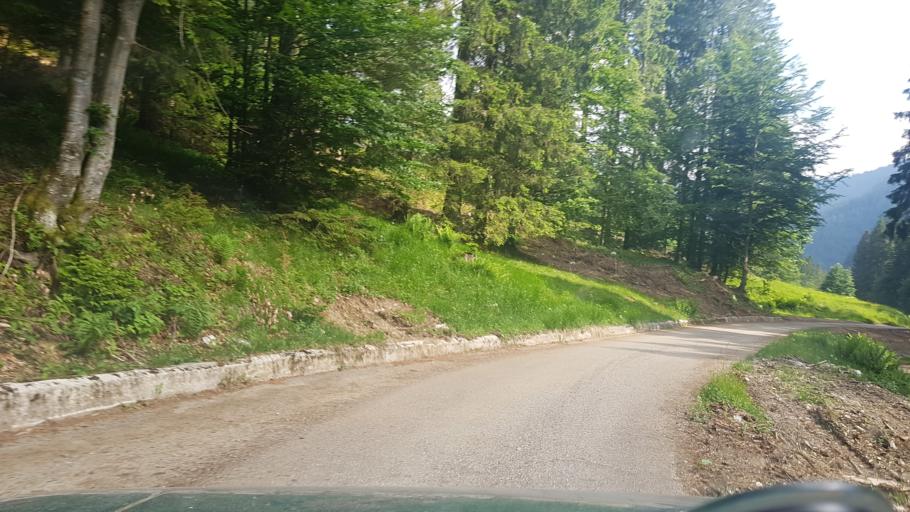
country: IT
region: Friuli Venezia Giulia
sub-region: Provincia di Udine
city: Paularo
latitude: 46.5420
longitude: 13.2051
